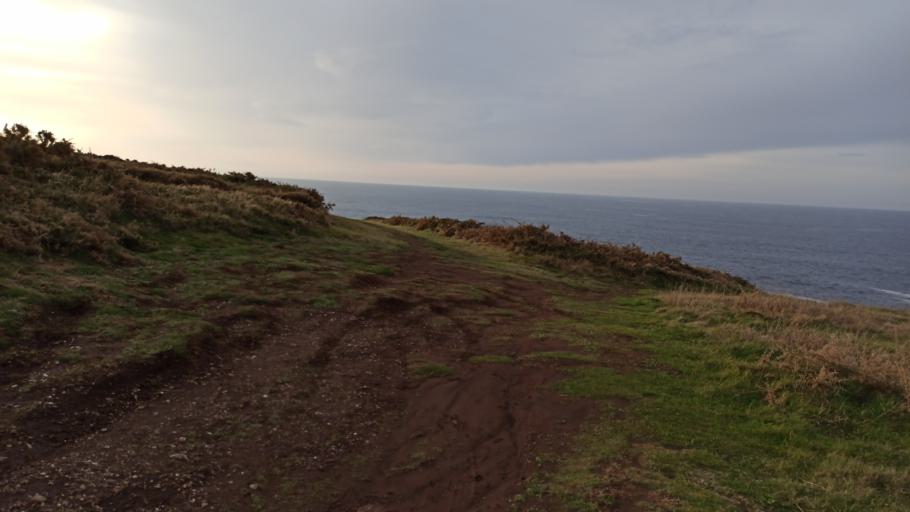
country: ES
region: Galicia
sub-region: Provincia da Coruna
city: A Coruna
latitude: 43.4005
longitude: -8.3333
